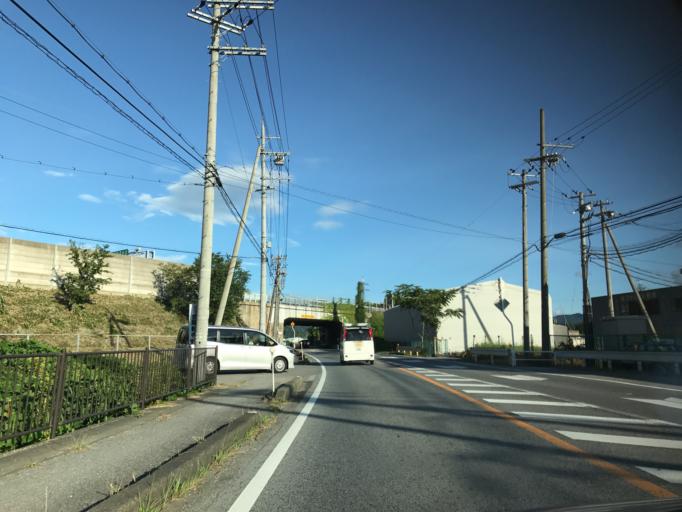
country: JP
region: Shiga Prefecture
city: Hikone
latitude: 35.2420
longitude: 136.2810
